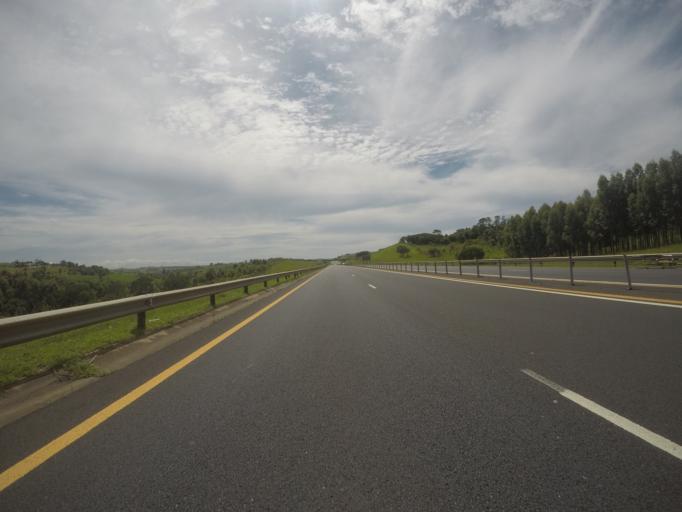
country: ZA
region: KwaZulu-Natal
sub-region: iLembe District Municipality
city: Mandeni
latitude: -29.1802
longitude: 31.4961
